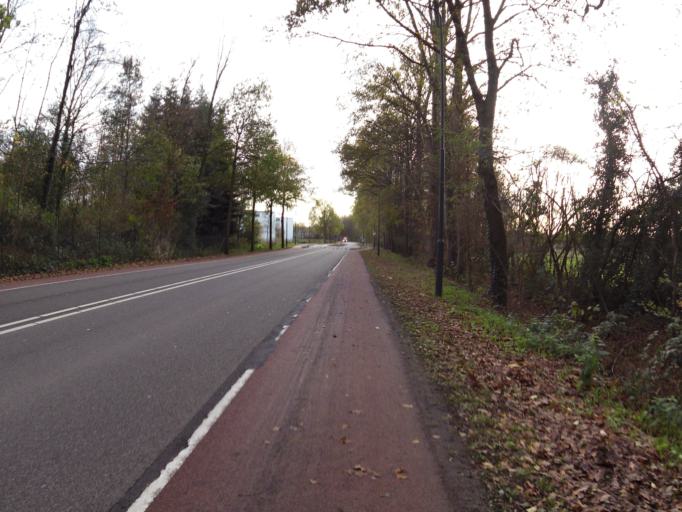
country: NL
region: North Brabant
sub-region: Gemeente Vught
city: Vught
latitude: 51.6457
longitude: 5.2725
